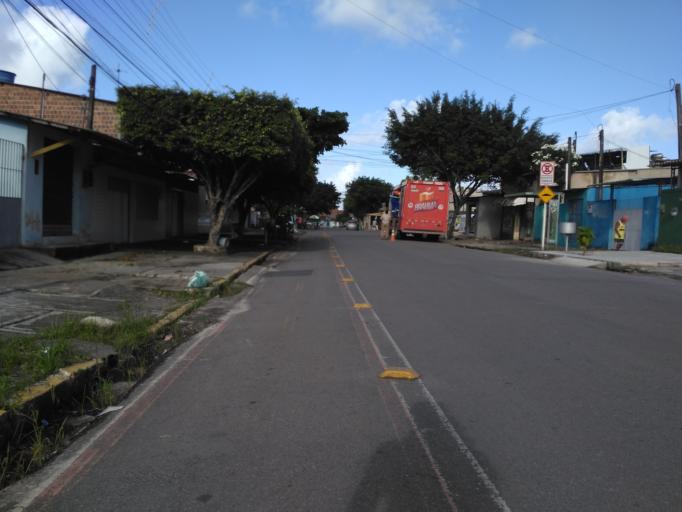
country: BR
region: Pernambuco
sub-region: Recife
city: Recife
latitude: -8.0605
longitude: -34.9432
